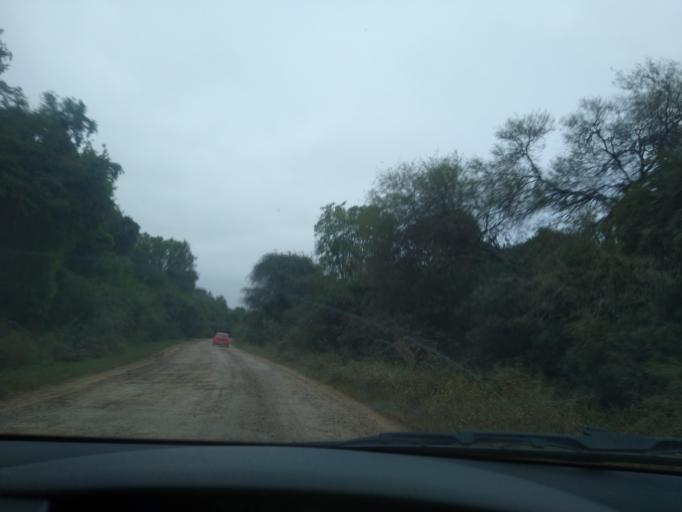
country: AR
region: Chaco
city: Colonia Benitez
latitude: -27.3373
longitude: -58.9676
